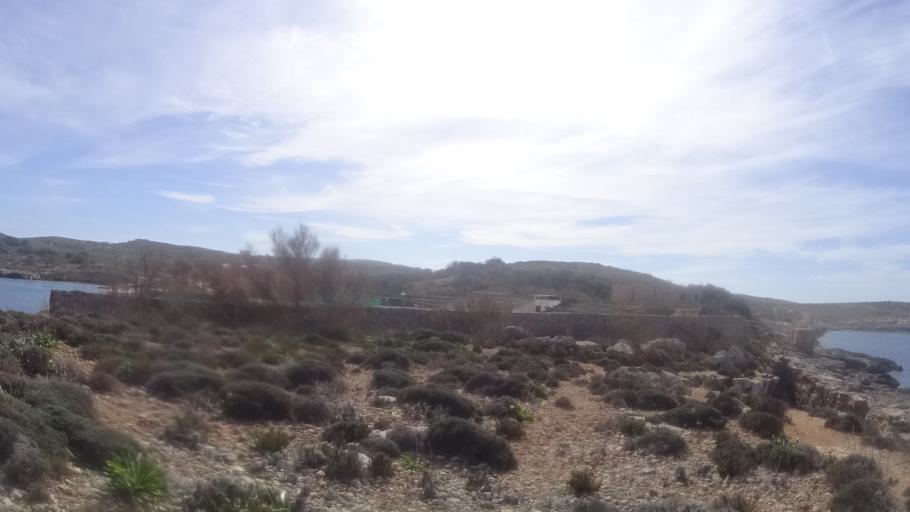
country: MT
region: Il-Qala
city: Qala
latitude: 36.0191
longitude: 14.3282
